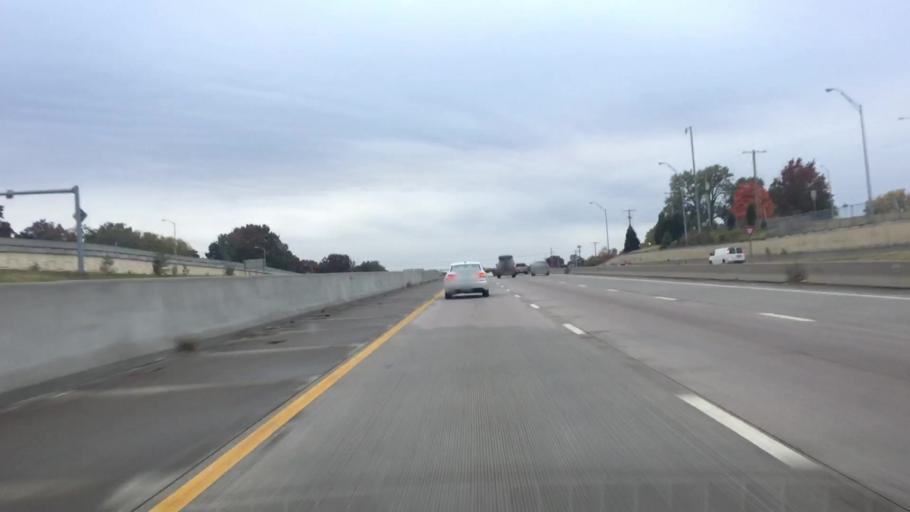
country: US
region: Kansas
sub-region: Johnson County
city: Lenexa
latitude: 38.9702
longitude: -94.7164
